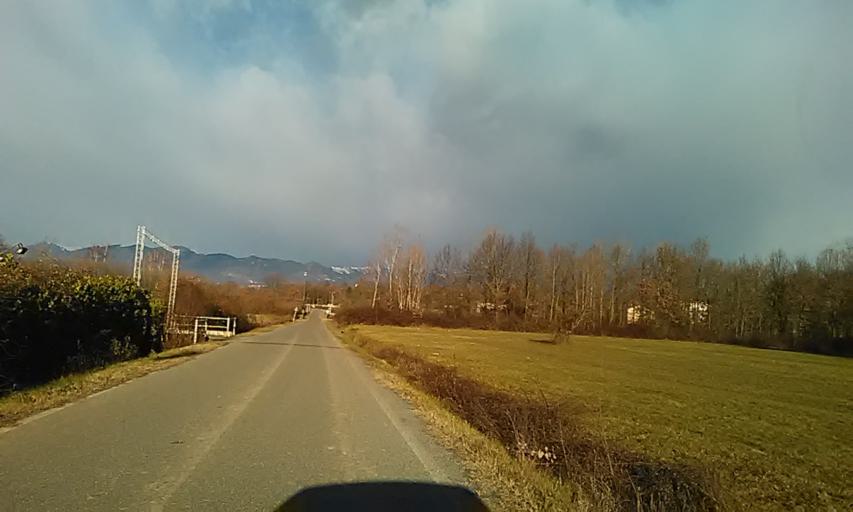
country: IT
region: Piedmont
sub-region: Provincia di Biella
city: Brusnengo
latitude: 45.5783
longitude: 8.2651
